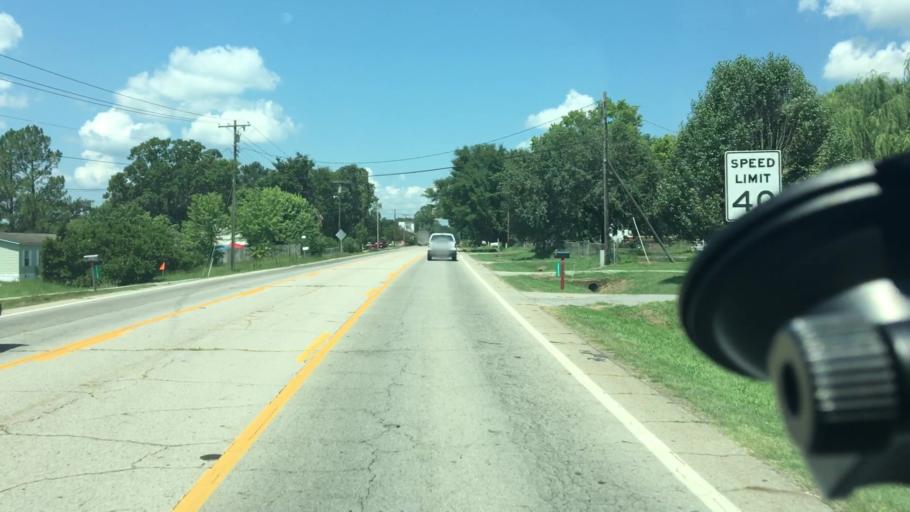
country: US
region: Arkansas
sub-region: Sebastian County
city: Lavaca
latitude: 35.2931
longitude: -94.1354
